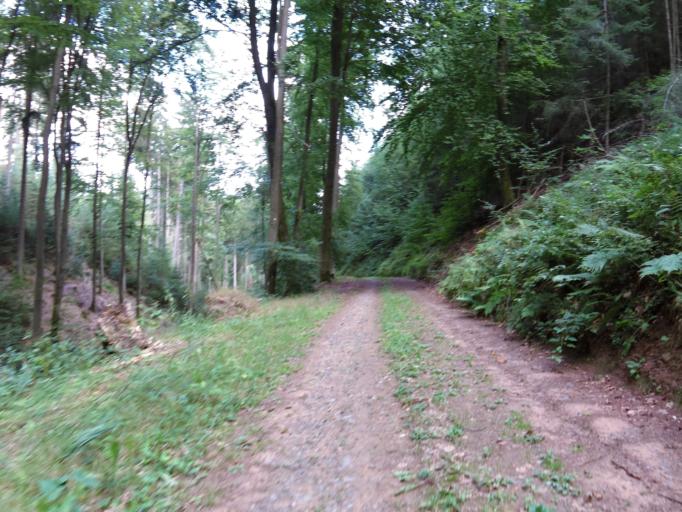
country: DE
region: Rheinland-Pfalz
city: Frankenstein
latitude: 49.4621
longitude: 8.0163
